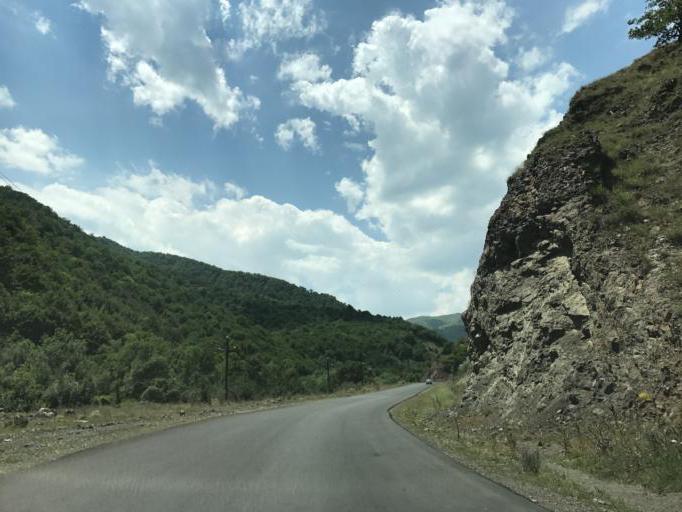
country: AZ
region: Kalbacar Rayonu
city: Kerbakhiar
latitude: 40.2324
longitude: 46.1125
